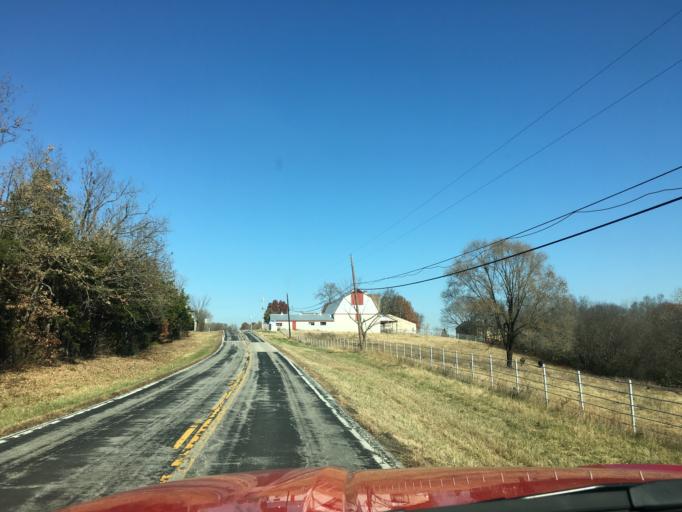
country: US
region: Missouri
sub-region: Cole County
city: Wardsville
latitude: 38.4775
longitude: -92.1771
